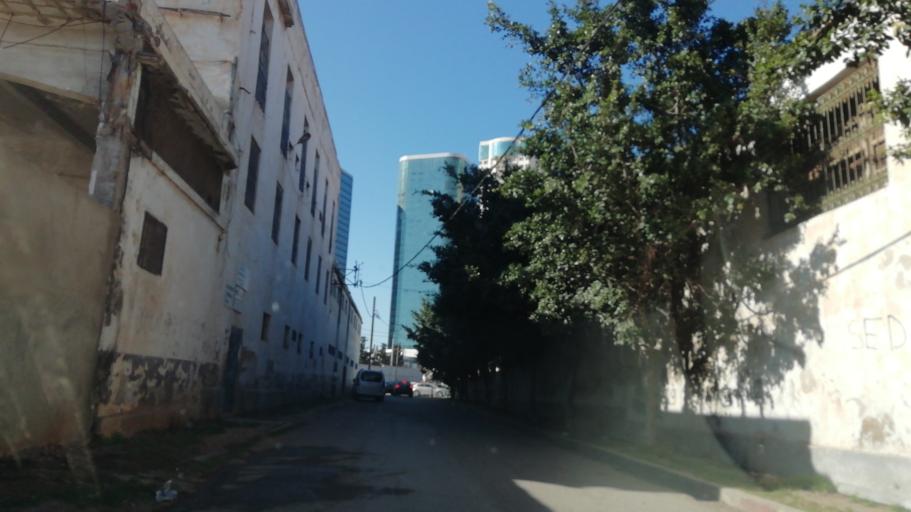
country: DZ
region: Oran
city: Oran
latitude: 35.7100
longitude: -0.6218
